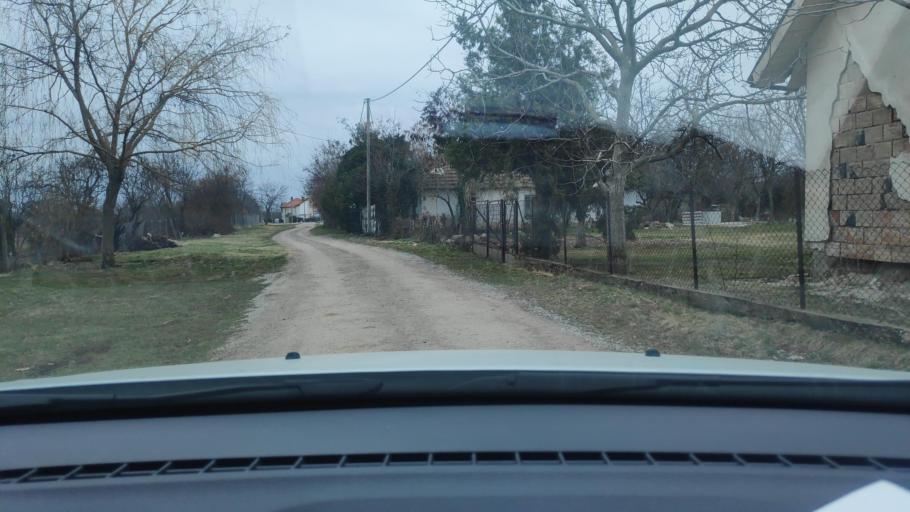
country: MK
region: Opstina Lipkovo
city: Matejche
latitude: 42.0862
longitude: 21.6191
